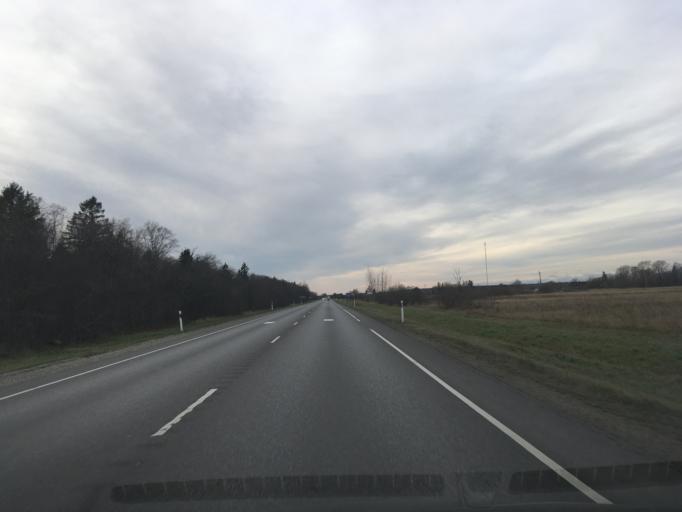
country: EE
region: Ida-Virumaa
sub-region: Kohtla-Jaerve linn
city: Kohtla-Jarve
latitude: 59.4210
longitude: 27.2230
